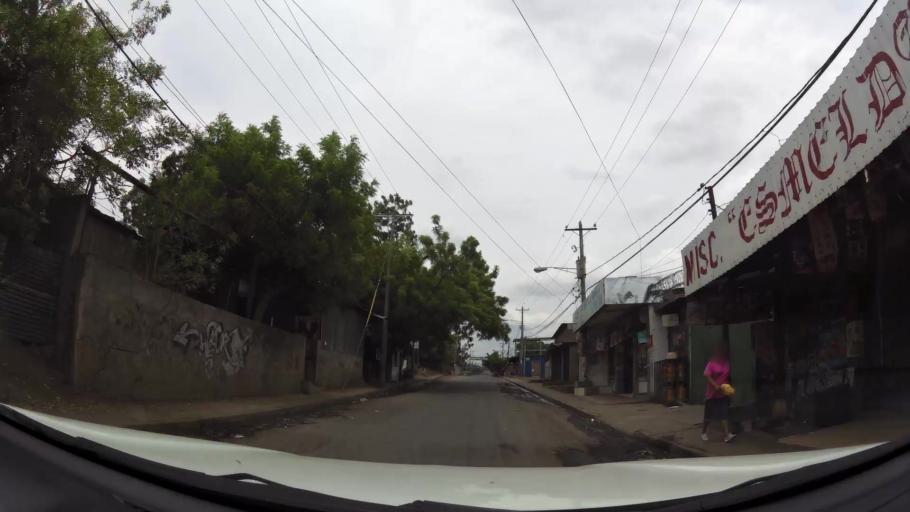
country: NI
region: Managua
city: Managua
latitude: 12.1215
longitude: -86.2160
